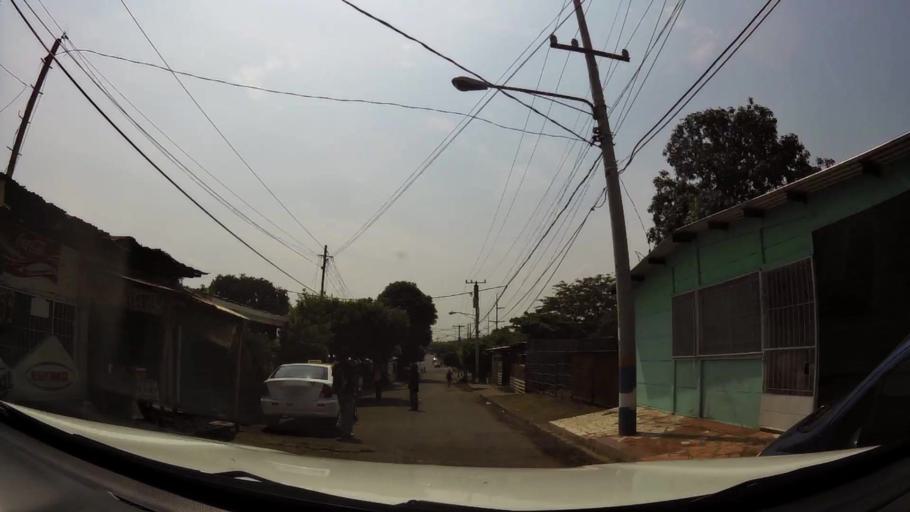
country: NI
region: Managua
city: Ciudad Sandino
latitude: 12.1237
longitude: -86.3140
